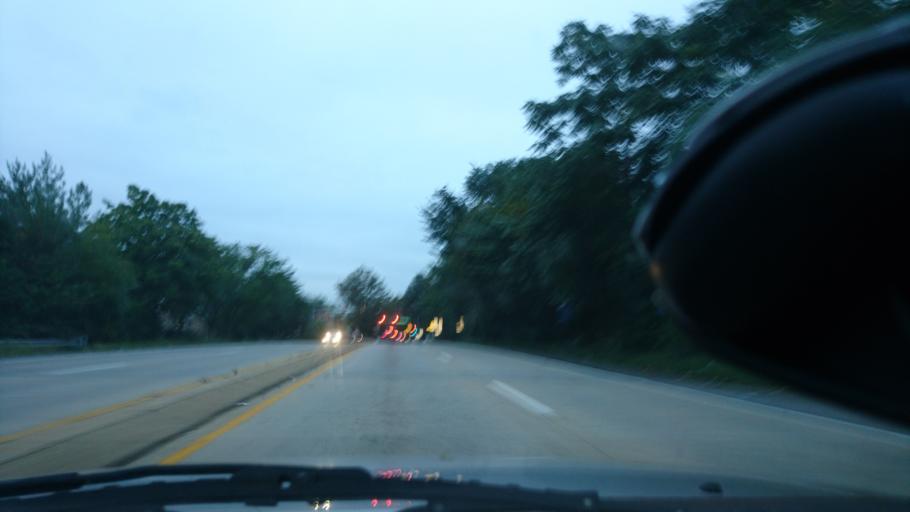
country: US
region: Pennsylvania
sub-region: Delaware County
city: Ridley Park
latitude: 39.8730
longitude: -75.3253
